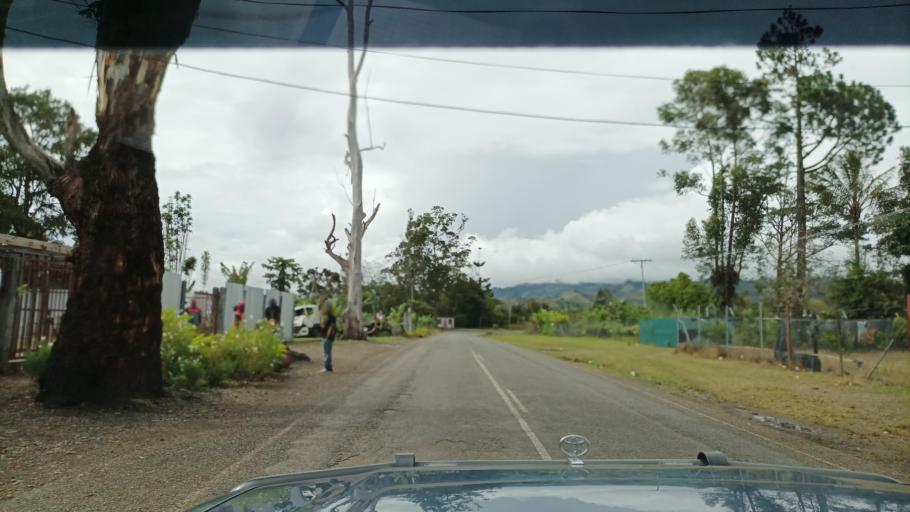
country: PG
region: Jiwaka
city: Minj
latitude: -5.9049
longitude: 144.6904
